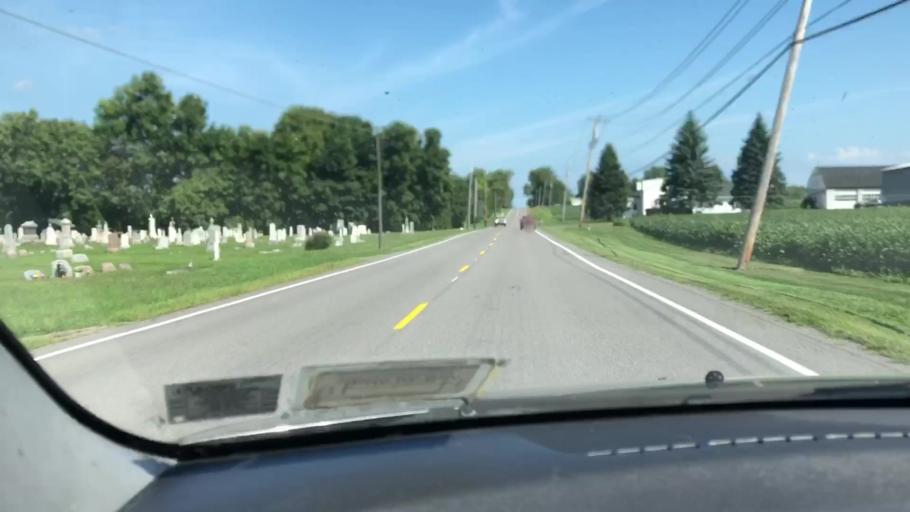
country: US
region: New York
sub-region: Wayne County
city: Macedon
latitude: 43.1036
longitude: -77.3207
